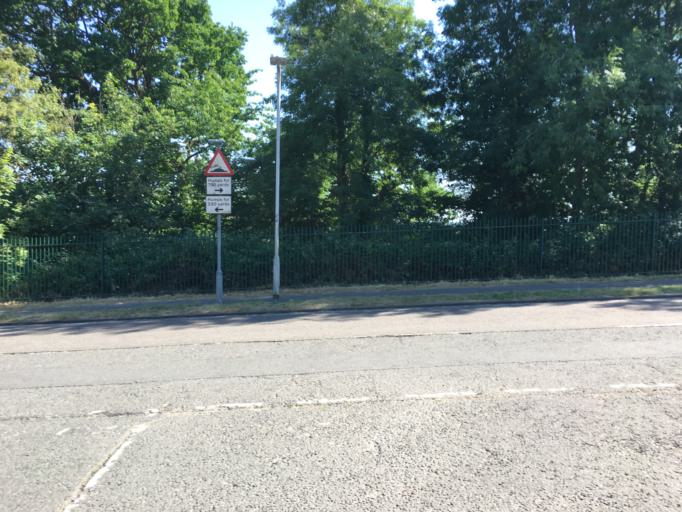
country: GB
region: England
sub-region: West Berkshire
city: Tilehurst
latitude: 51.4481
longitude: -1.0204
